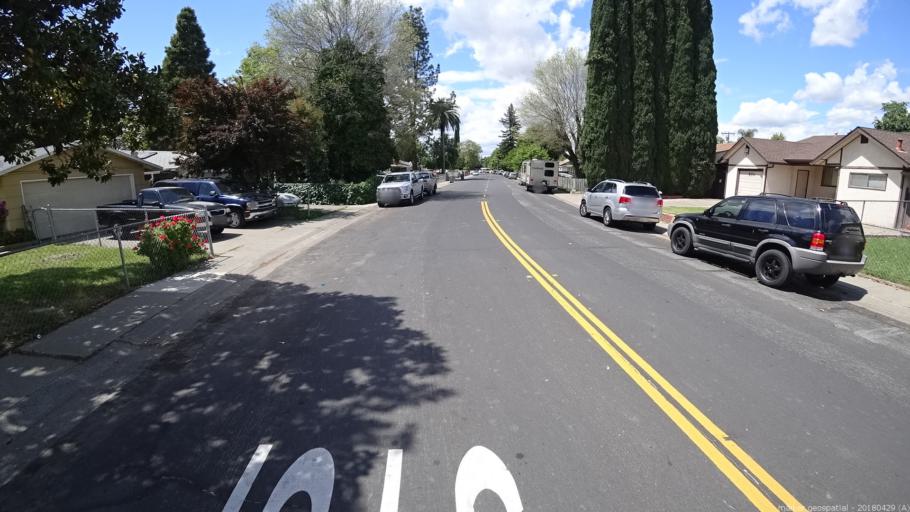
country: US
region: California
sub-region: Yolo County
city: West Sacramento
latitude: 38.5963
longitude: -121.5230
